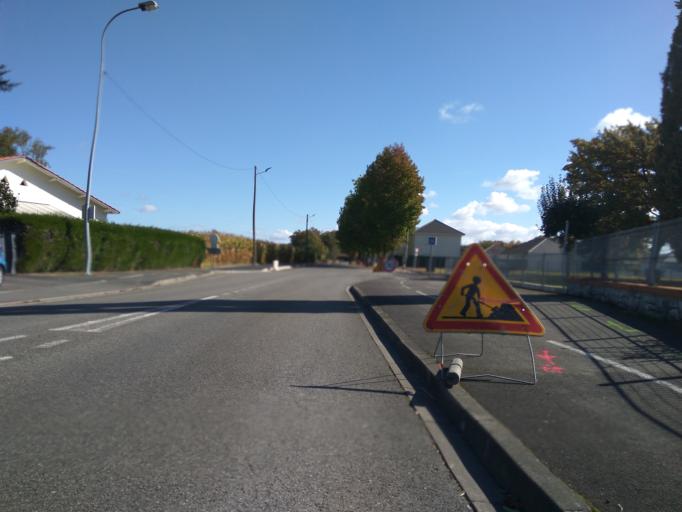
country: FR
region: Aquitaine
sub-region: Departement des Pyrenees-Atlantiques
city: Idron
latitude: 43.2992
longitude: -0.3181
